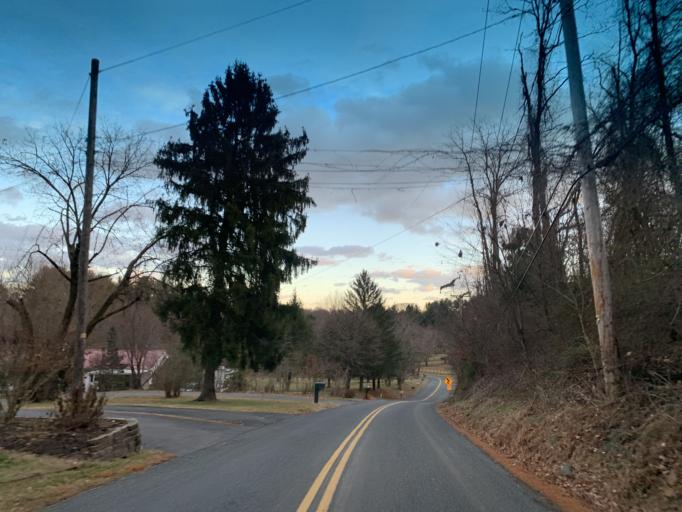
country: US
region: Pennsylvania
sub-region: York County
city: Susquehanna Trails
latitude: 39.6584
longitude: -76.3076
